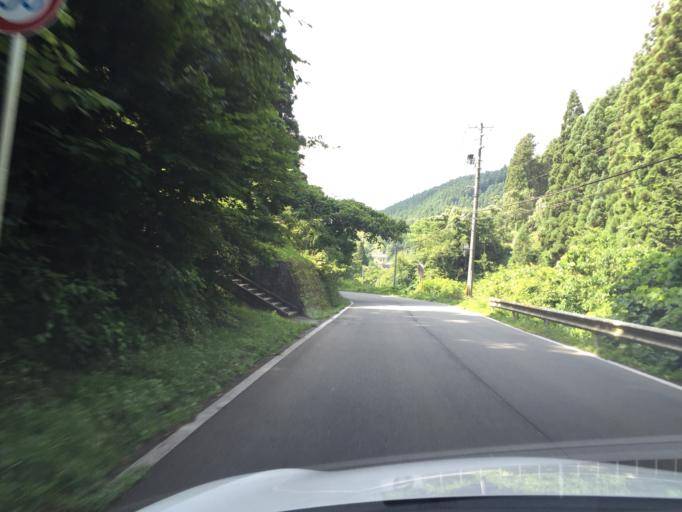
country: JP
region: Fukushima
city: Iwaki
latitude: 36.9985
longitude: 140.7107
